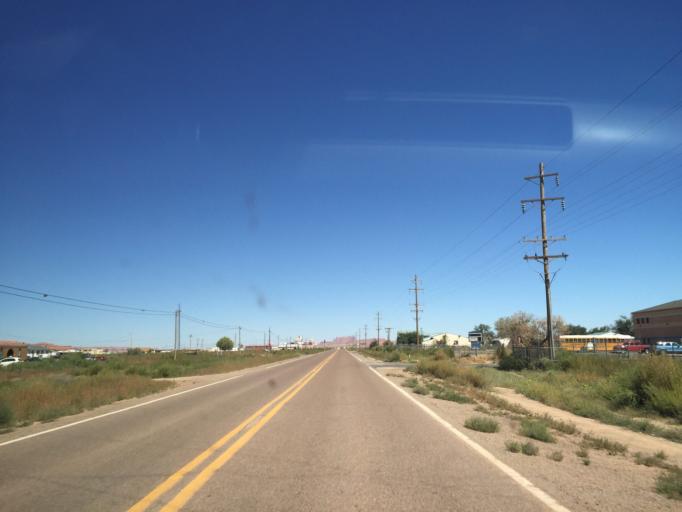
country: US
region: Arizona
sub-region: Apache County
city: Many Farms
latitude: 36.3477
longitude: -109.6201
